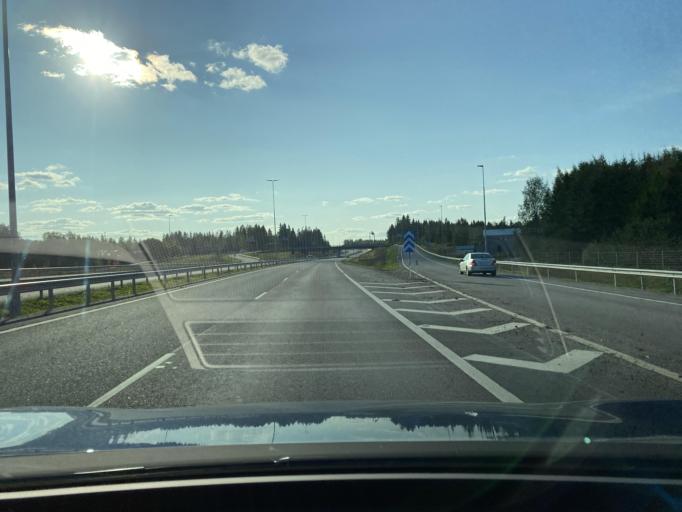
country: FI
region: Paijanne Tavastia
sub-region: Lahti
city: Lahti
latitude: 60.9547
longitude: 25.6243
